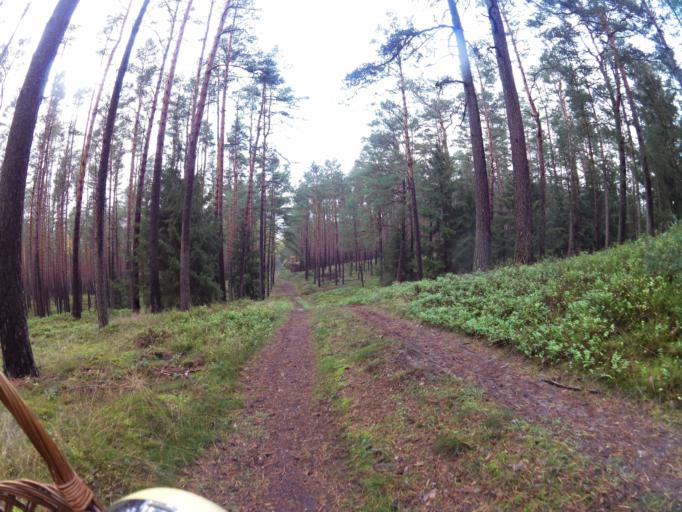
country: PL
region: West Pomeranian Voivodeship
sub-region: Powiat policki
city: Nowe Warpno
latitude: 53.6164
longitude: 14.3450
